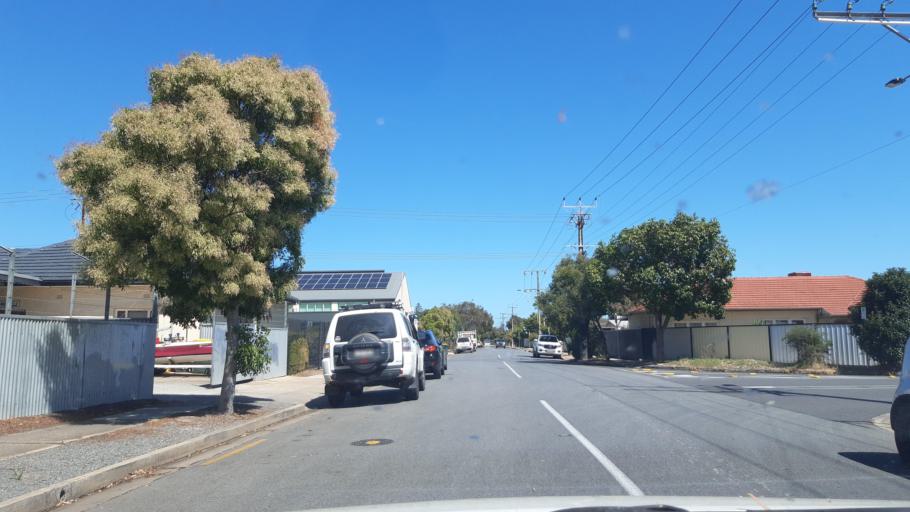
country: AU
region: South Australia
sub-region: Marion
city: Clovelly Park
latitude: -34.9911
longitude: 138.5718
